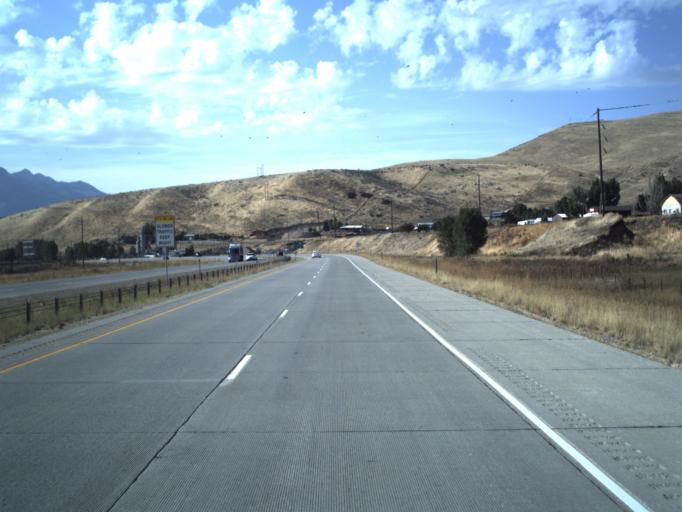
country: US
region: Utah
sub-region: Morgan County
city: Mountain Green
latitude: 41.1066
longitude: -111.7476
